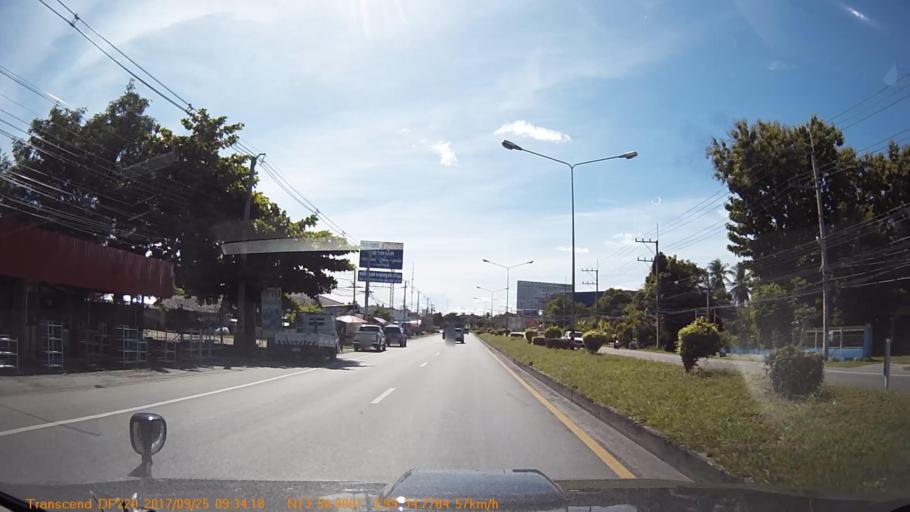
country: TH
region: Kanchanaburi
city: Kanchanaburi
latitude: 13.9817
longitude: 99.5795
